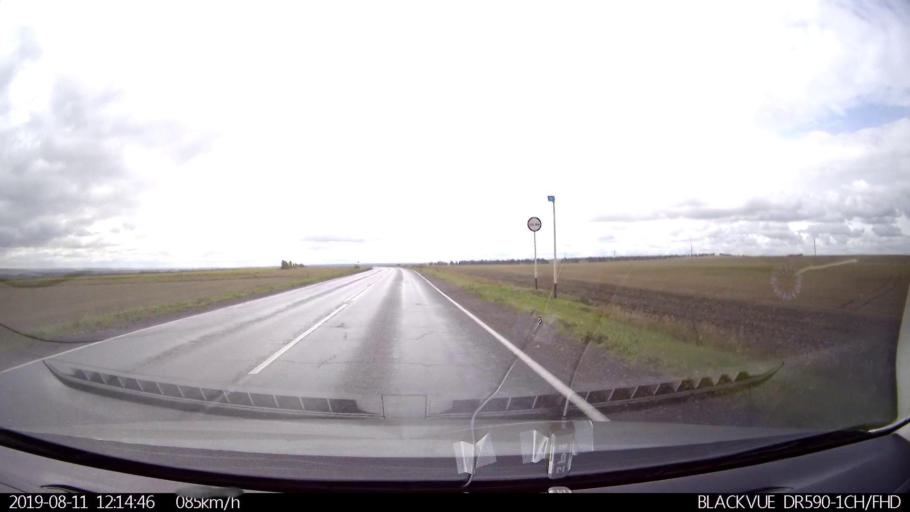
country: RU
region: Ulyanovsk
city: Ignatovka
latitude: 53.9489
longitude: 47.9756
